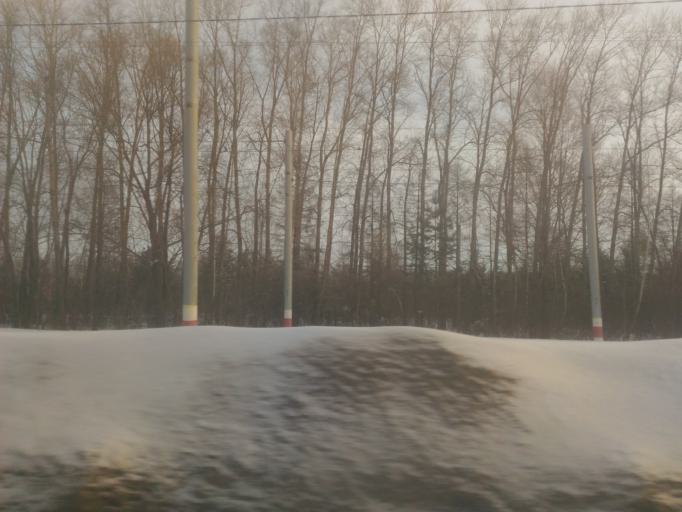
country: RU
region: Ulyanovsk
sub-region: Ulyanovskiy Rayon
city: Ulyanovsk
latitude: 54.3623
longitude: 48.3379
